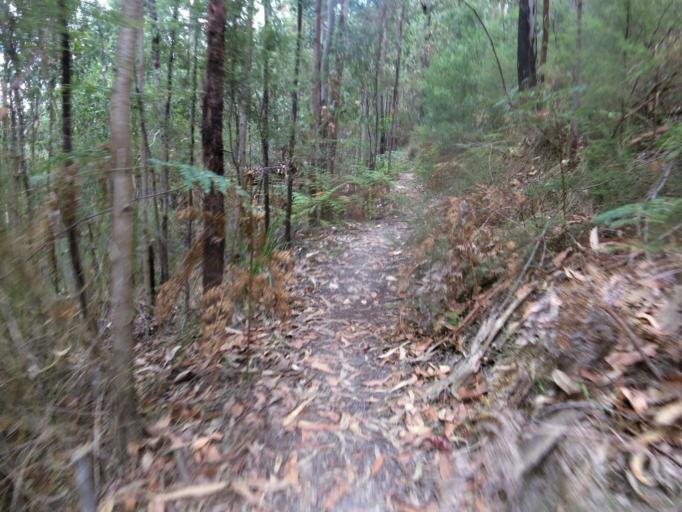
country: AU
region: Victoria
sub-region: Nillumbik
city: Saint Andrews
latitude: -37.5454
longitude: 145.3469
